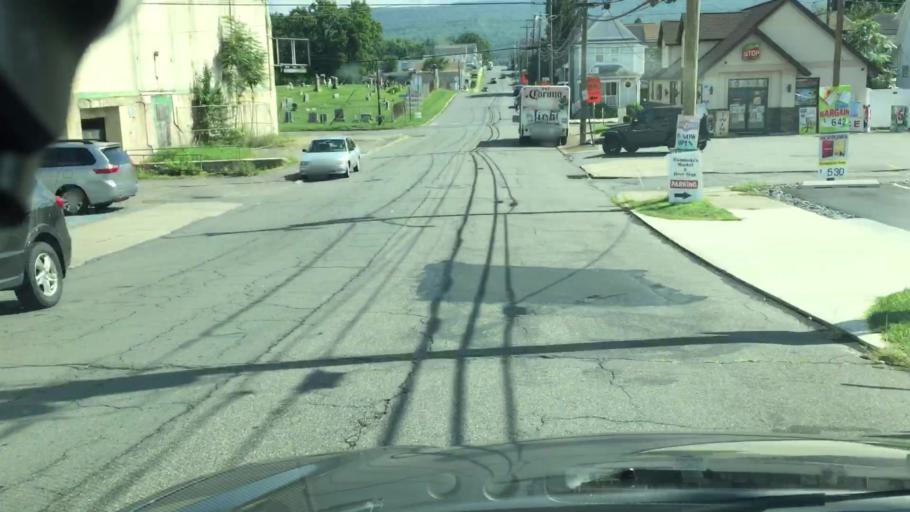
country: US
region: Pennsylvania
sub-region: Luzerne County
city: Nanticoke
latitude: 41.1977
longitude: -75.9993
